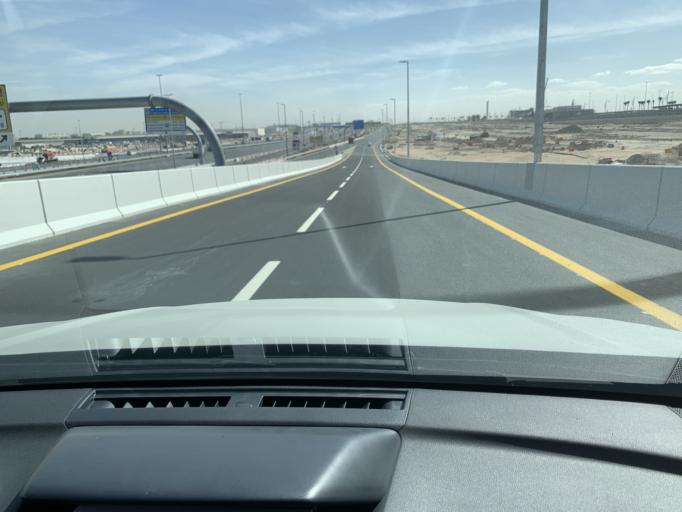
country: AE
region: Dubai
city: Dubai
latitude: 24.9713
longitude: 55.1517
